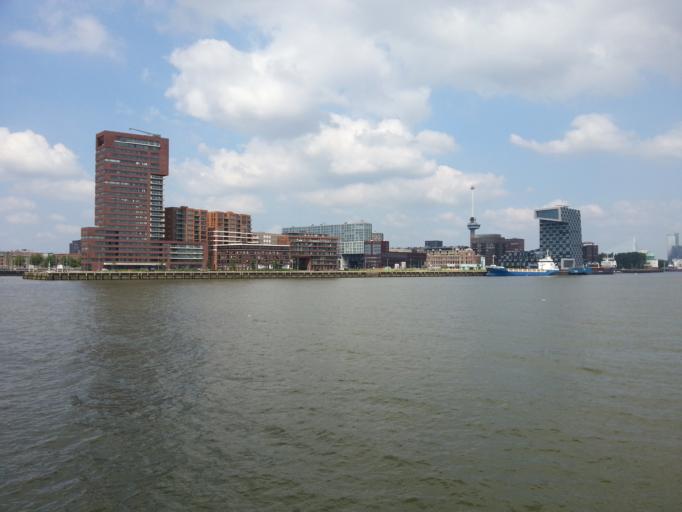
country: NL
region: South Holland
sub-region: Gemeente Rotterdam
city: Delfshaven
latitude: 51.8984
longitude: 4.4534
